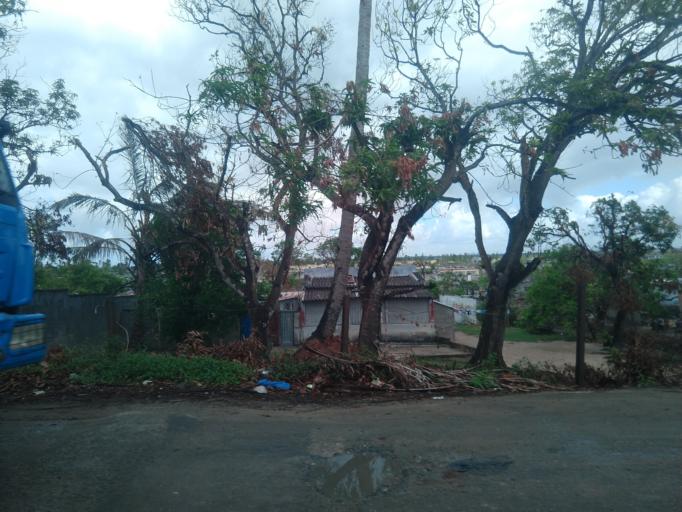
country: MZ
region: Sofala
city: Beira
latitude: -19.7970
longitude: 34.8937
